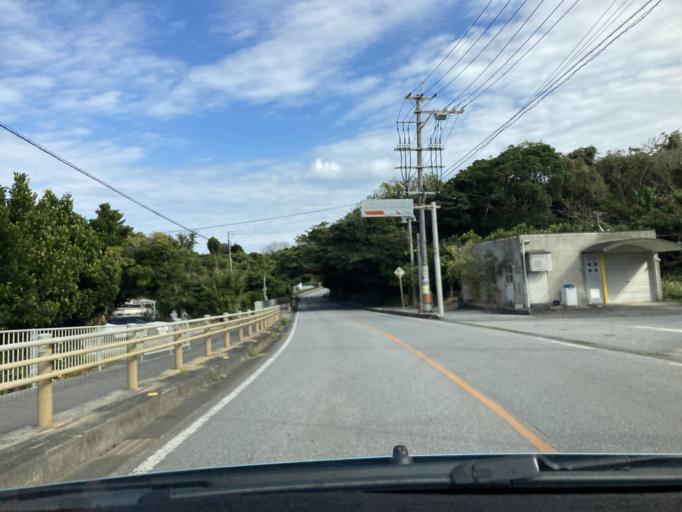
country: JP
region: Okinawa
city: Nago
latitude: 26.6962
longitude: 127.9439
